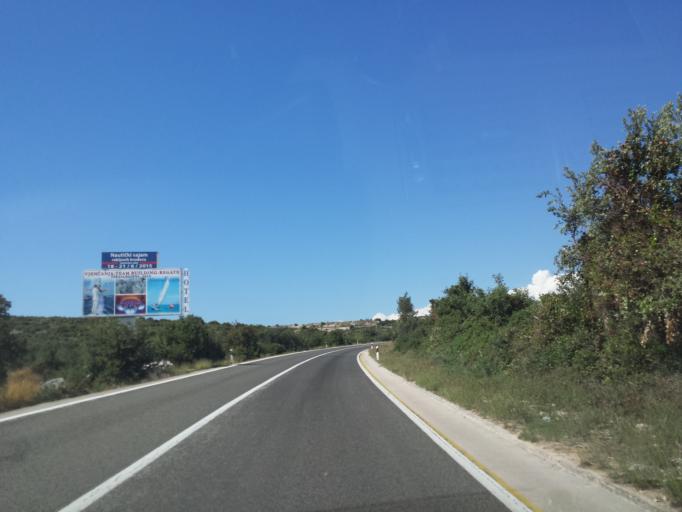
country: HR
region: Sibensko-Kniniska
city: Rogoznica
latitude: 43.5462
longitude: 15.9617
